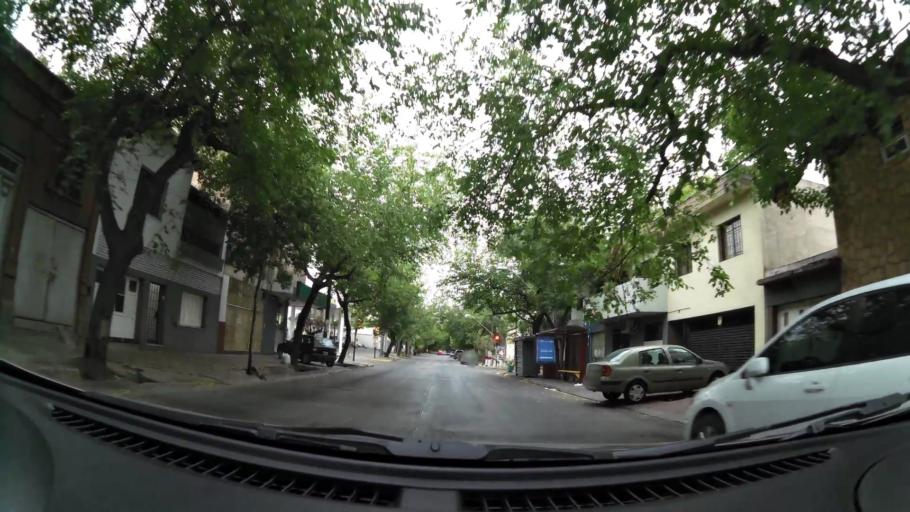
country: AR
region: Mendoza
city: Mendoza
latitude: -32.8786
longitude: -68.8570
